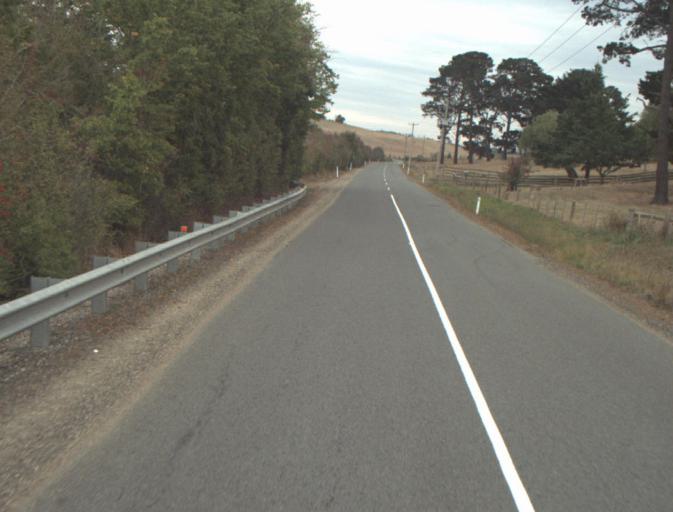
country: AU
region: Tasmania
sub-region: Northern Midlands
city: Evandale
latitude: -41.5278
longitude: 147.2333
